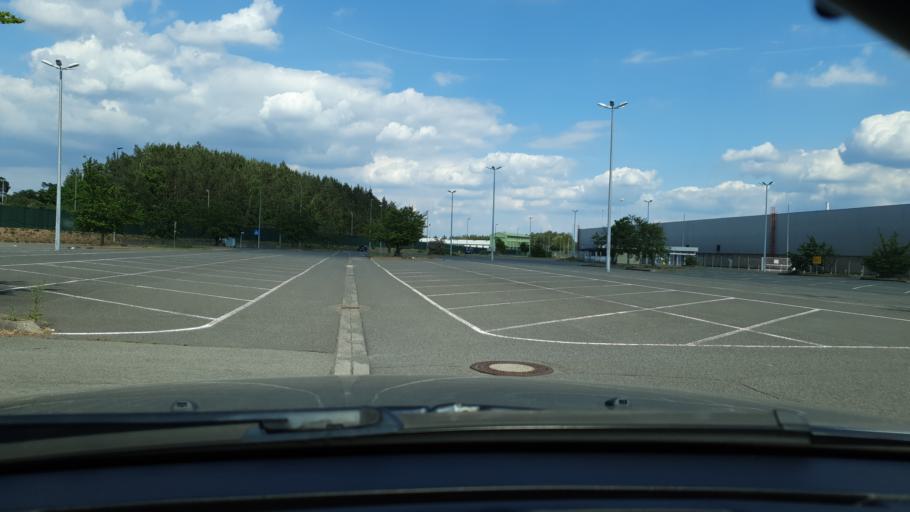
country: DE
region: Rheinland-Pfalz
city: Rodenbach
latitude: 49.4421
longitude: 7.6841
